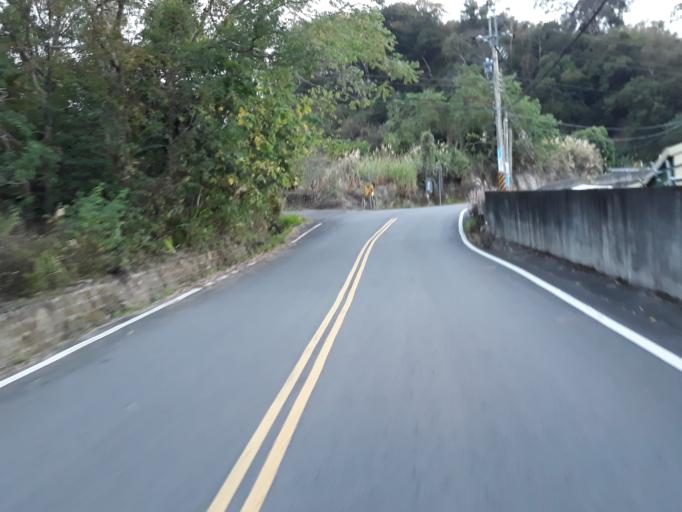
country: TW
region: Taiwan
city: Fengyuan
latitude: 24.3738
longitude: 120.8636
